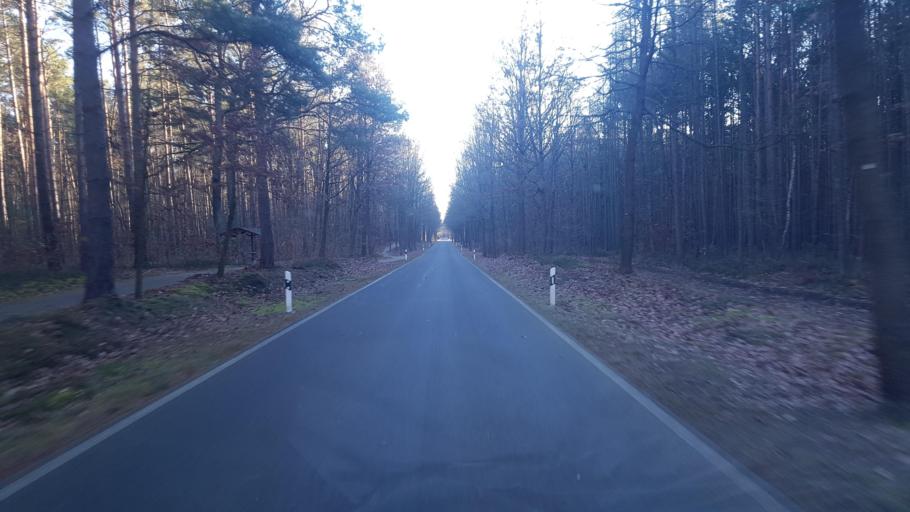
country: DE
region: Brandenburg
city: Tauer
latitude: 51.9244
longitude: 14.4886
